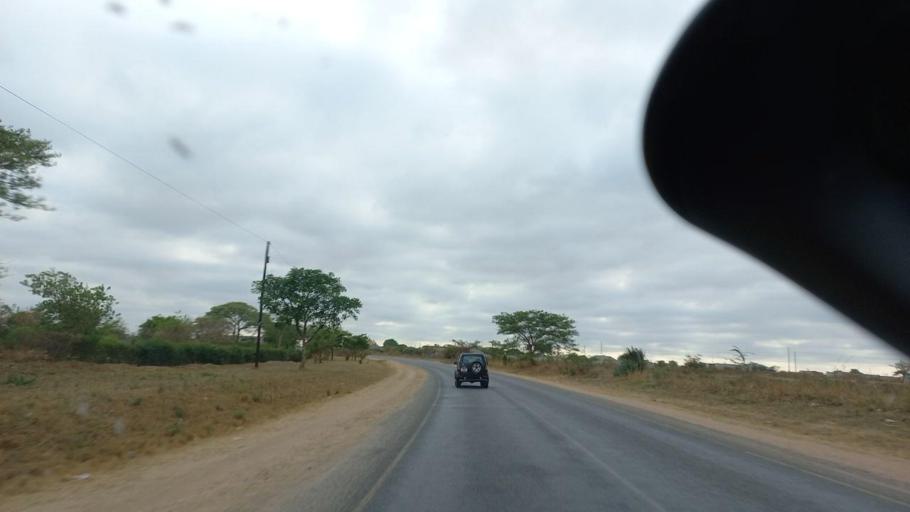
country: ZM
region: Lusaka
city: Chongwe
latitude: -15.3466
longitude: 28.6563
